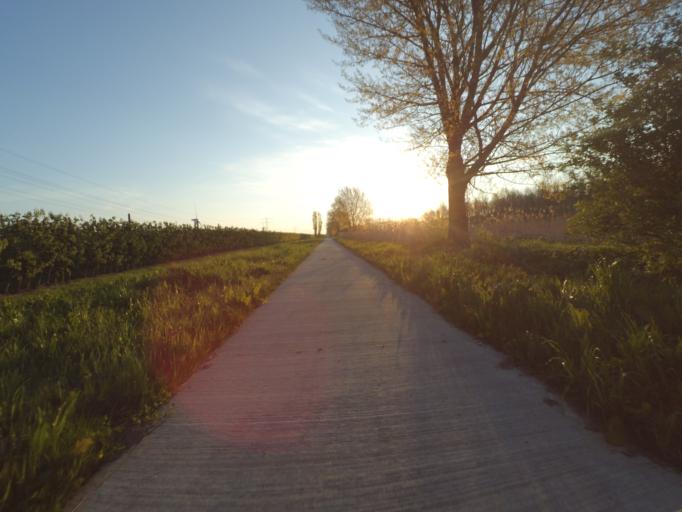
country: NL
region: Flevoland
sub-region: Gemeente Zeewolde
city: Zeewolde
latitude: 52.3482
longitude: 5.4701
